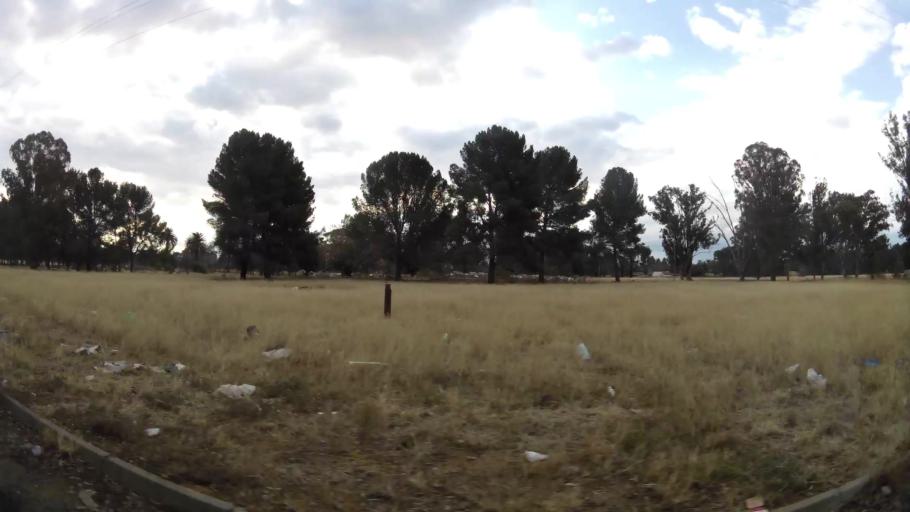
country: ZA
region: Orange Free State
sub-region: Lejweleputswa District Municipality
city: Welkom
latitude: -27.9997
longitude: 26.7190
